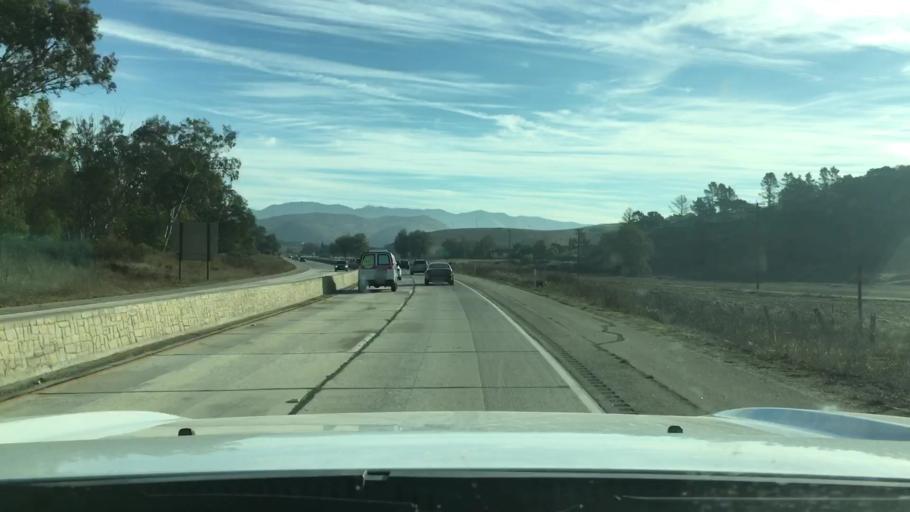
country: US
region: California
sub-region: San Luis Obispo County
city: San Luis Obispo
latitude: 35.3196
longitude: -120.7117
